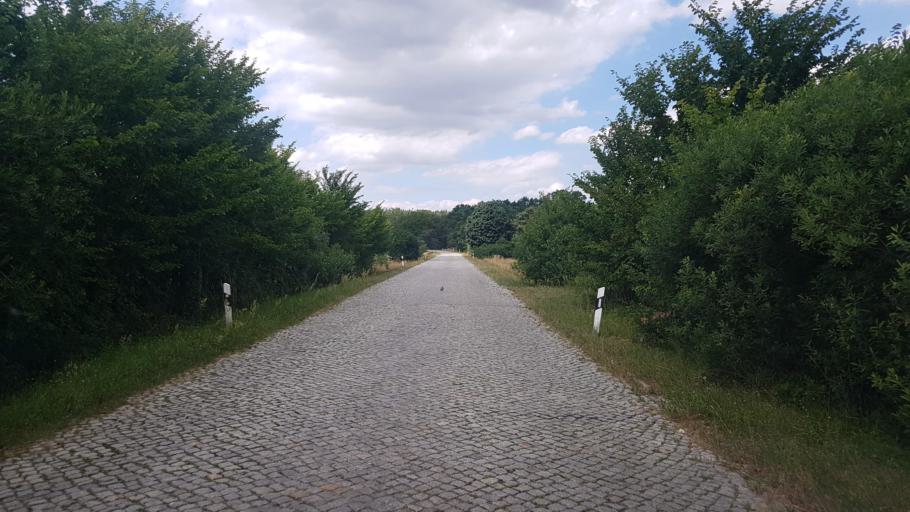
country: DE
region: Brandenburg
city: Juterbog
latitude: 52.0404
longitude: 13.1234
